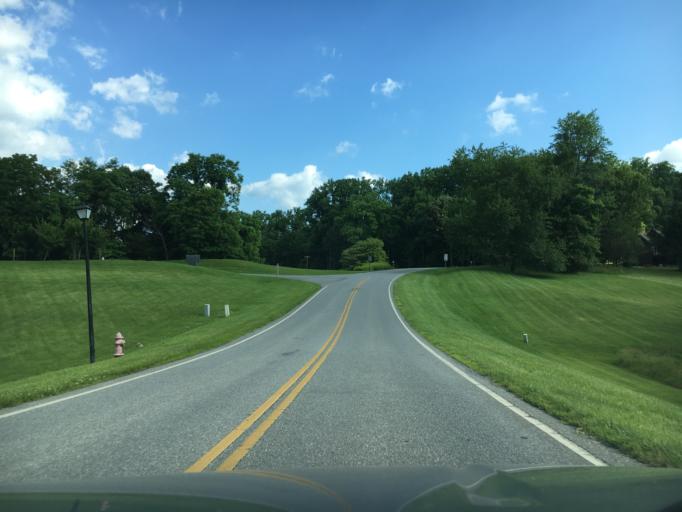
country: US
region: Virginia
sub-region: Bedford County
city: Forest
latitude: 37.3937
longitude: -79.2552
